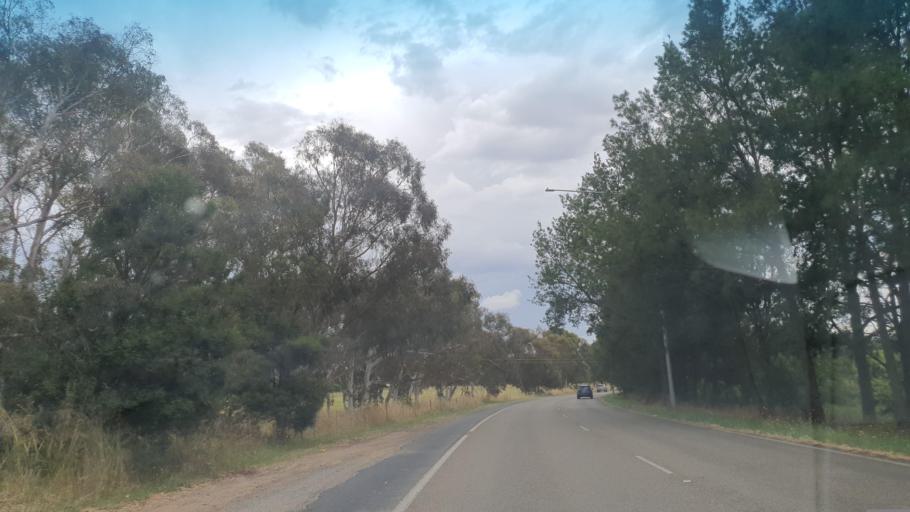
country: AU
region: Australian Capital Territory
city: Macquarie
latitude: -35.2144
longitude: 149.0388
